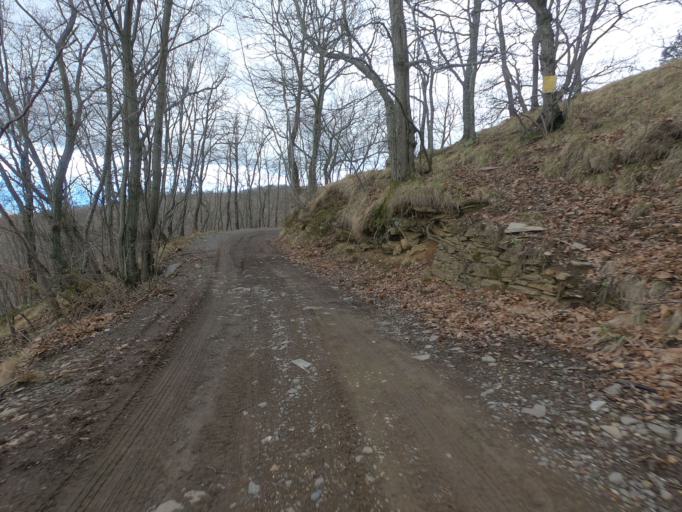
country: IT
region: Liguria
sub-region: Provincia di Imperia
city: Pietrabruna
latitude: 43.9169
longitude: 7.8822
